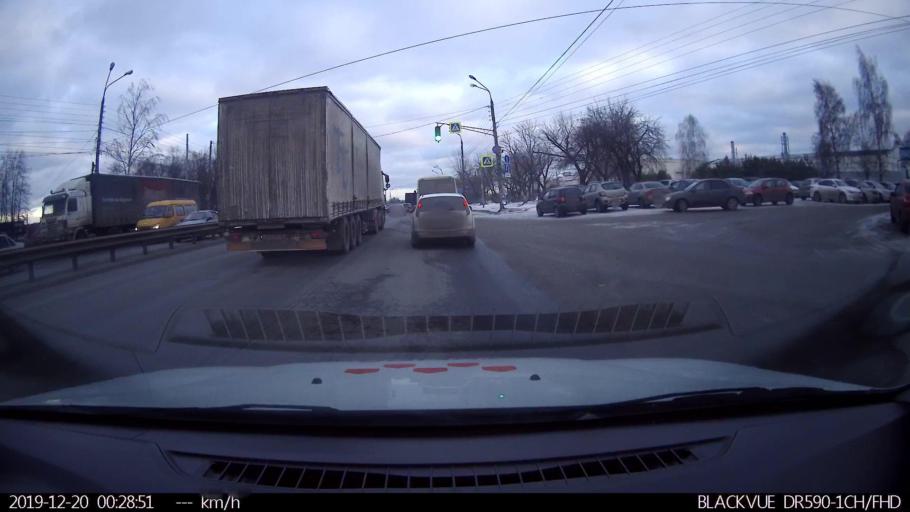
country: RU
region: Vladimir
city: Yur'yev-Pol'skiy
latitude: 56.5603
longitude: 39.6196
